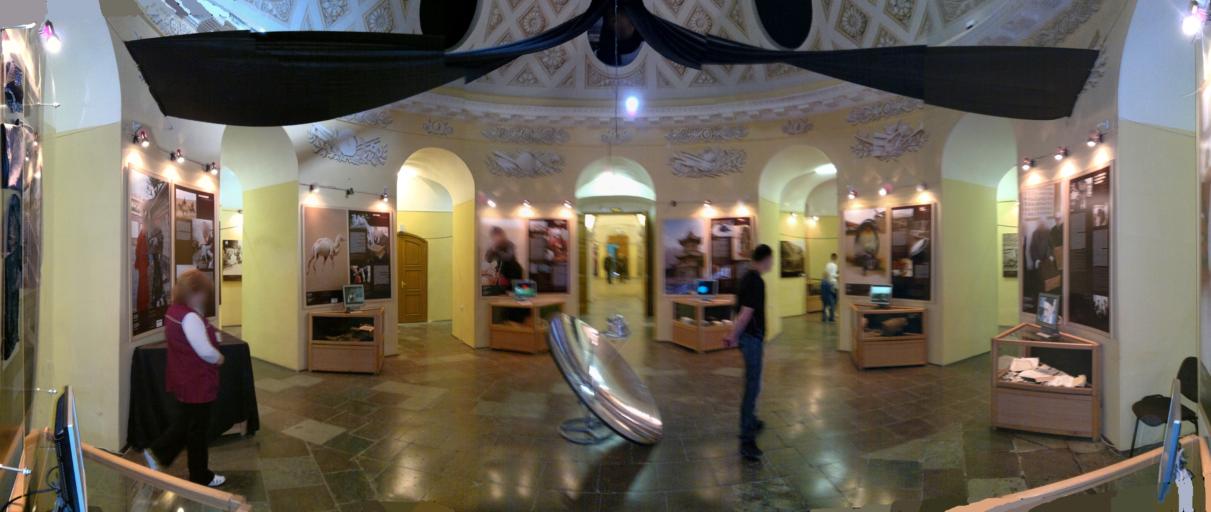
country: RU
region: St.-Petersburg
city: Saint Petersburg
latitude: 59.9415
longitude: 30.3046
